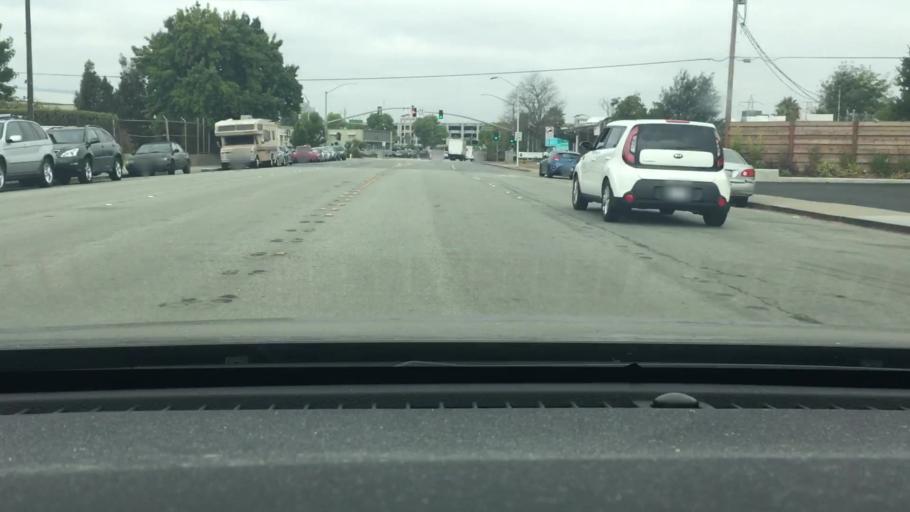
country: US
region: California
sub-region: San Mateo County
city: Millbrae
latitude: 37.5988
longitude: -122.3816
